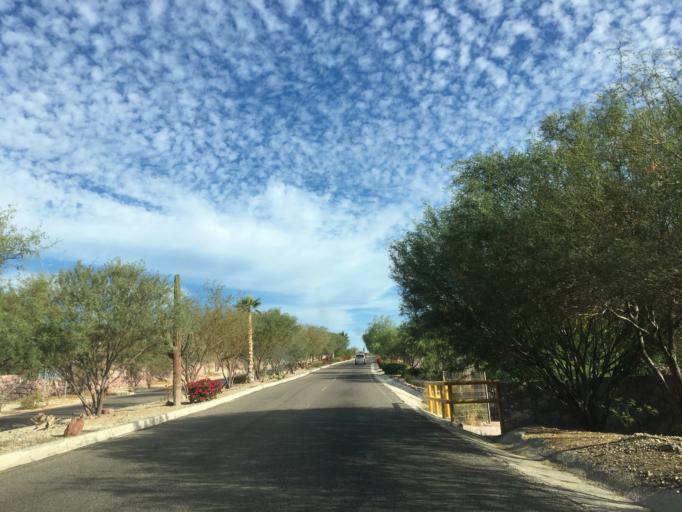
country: MX
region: Baja California Sur
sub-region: La Paz
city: La Paz
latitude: 24.2085
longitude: -110.2979
